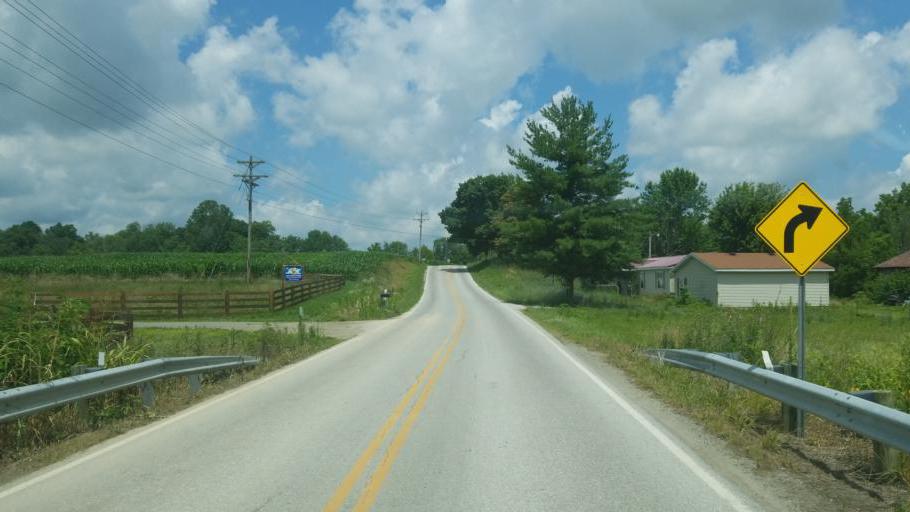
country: US
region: Ohio
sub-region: Highland County
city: Leesburg
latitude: 39.2537
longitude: -83.4731
